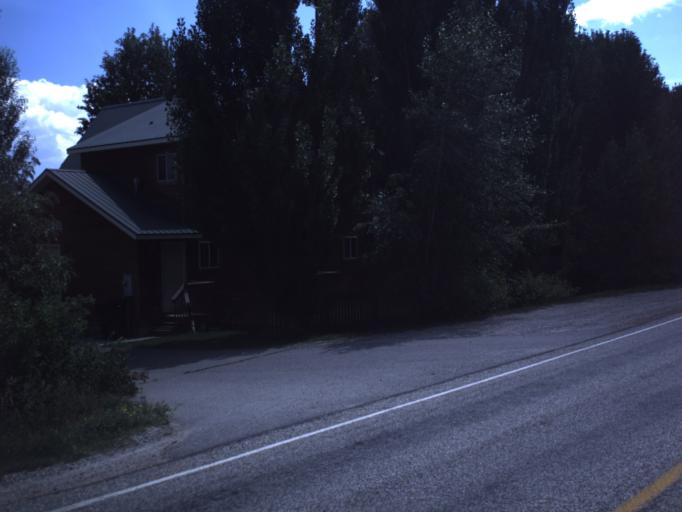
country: US
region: Idaho
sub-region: Bear Lake County
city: Paris
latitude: 41.9920
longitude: -111.4113
